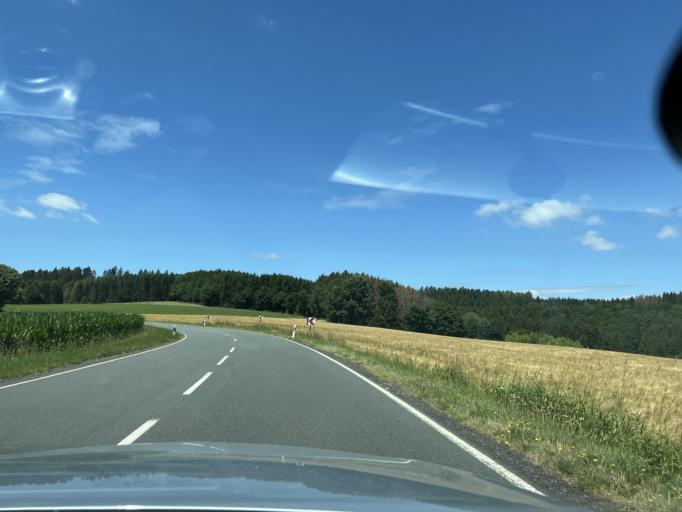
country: DE
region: North Rhine-Westphalia
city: Kreuztal
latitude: 50.9605
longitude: 7.9385
